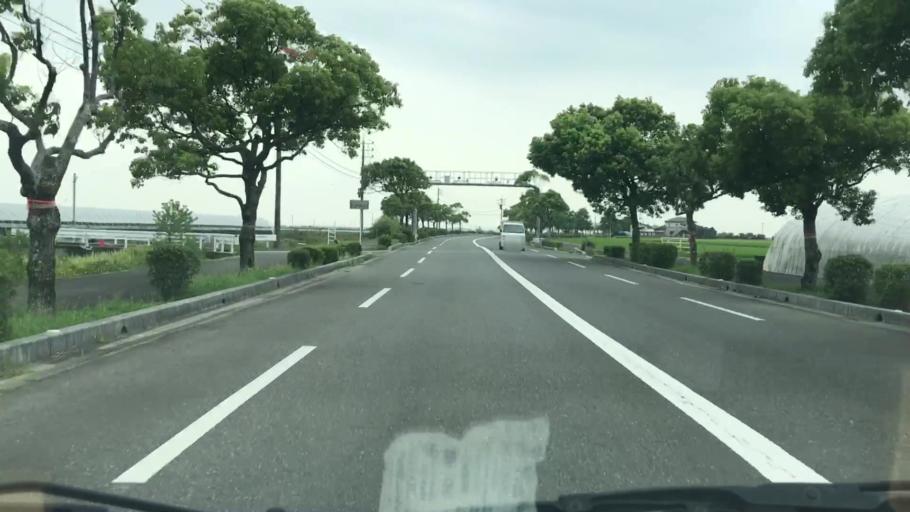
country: JP
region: Saga Prefecture
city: Okawa
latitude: 33.1940
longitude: 130.3036
